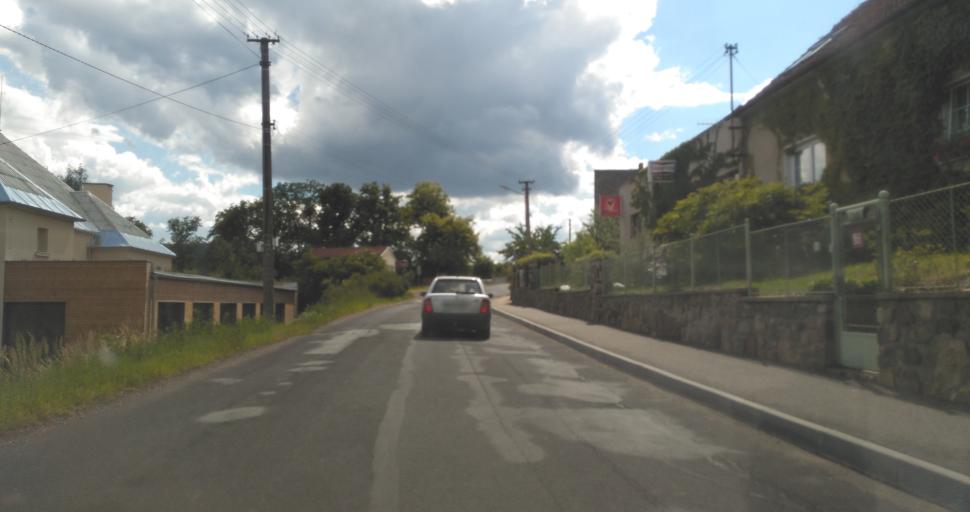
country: CZ
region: Plzensky
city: Zbiroh
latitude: 49.8549
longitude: 13.7669
